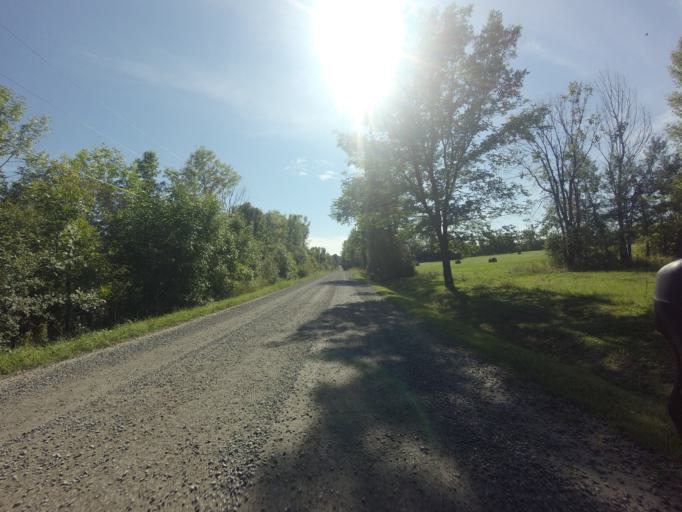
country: CA
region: Ontario
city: Perth
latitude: 44.9376
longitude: -76.3728
